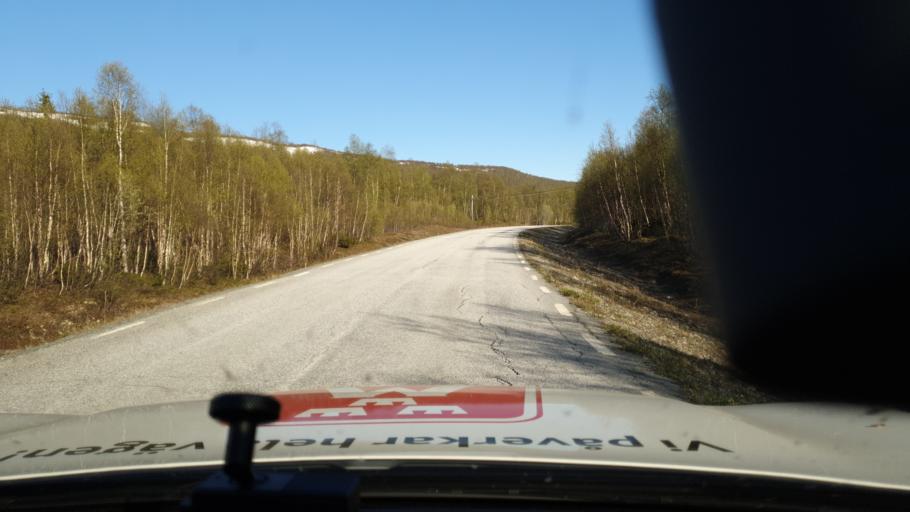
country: NO
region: Nordland
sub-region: Rana
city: Mo i Rana
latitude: 65.7801
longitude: 15.1285
